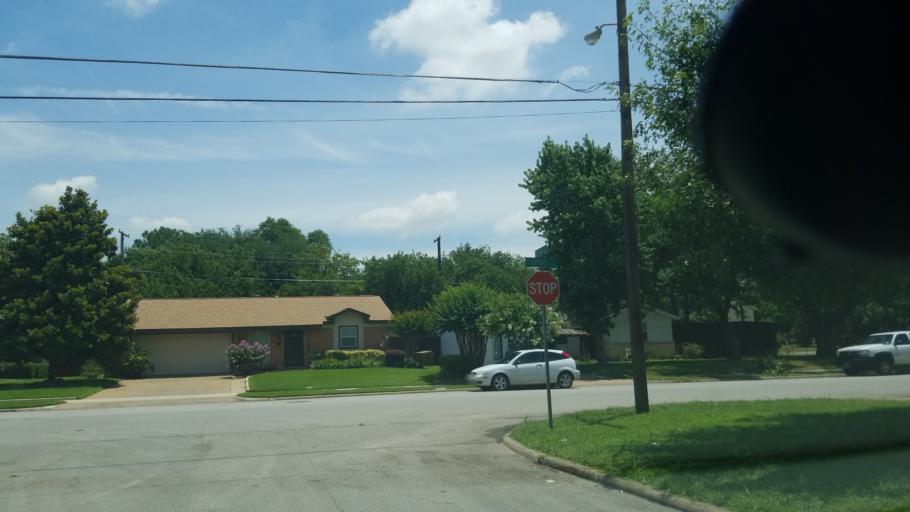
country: US
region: Texas
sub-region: Dallas County
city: Irving
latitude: 32.8441
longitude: -96.9684
